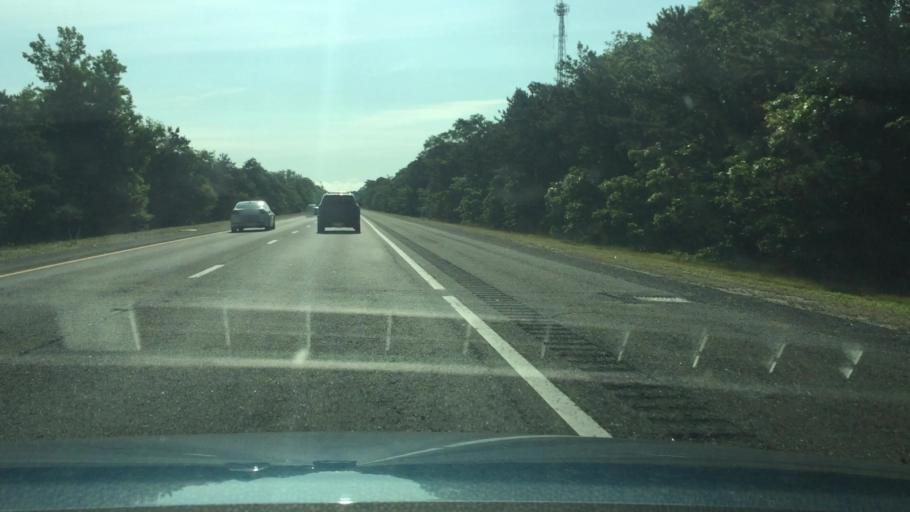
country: US
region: Massachusetts
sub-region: Barnstable County
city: South Yarmouth
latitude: 41.6912
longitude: -70.1938
